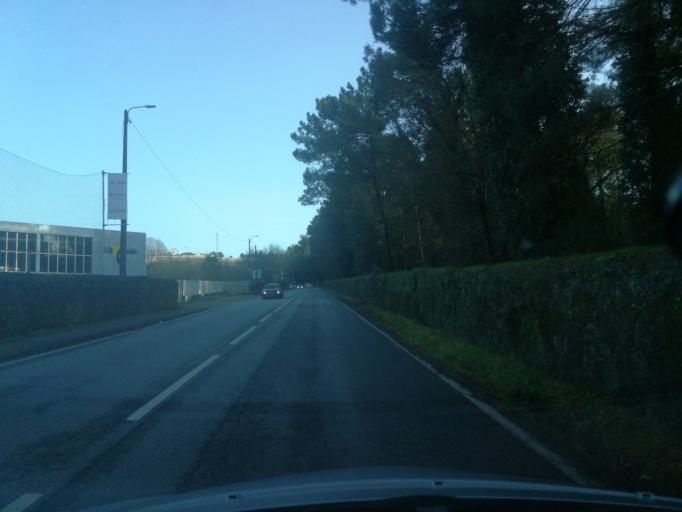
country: PT
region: Braga
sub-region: Barcelos
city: Barcelos
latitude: 41.5239
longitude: -8.6128
